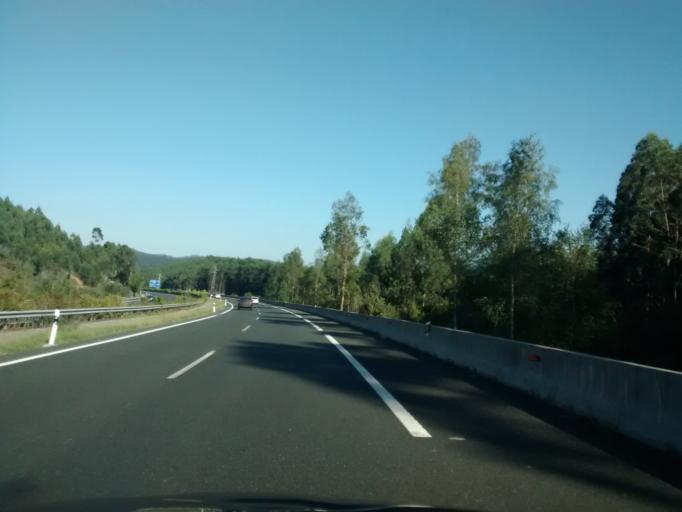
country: ES
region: Cantabria
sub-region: Provincia de Cantabria
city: Luzmela
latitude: 43.3206
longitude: -4.2120
